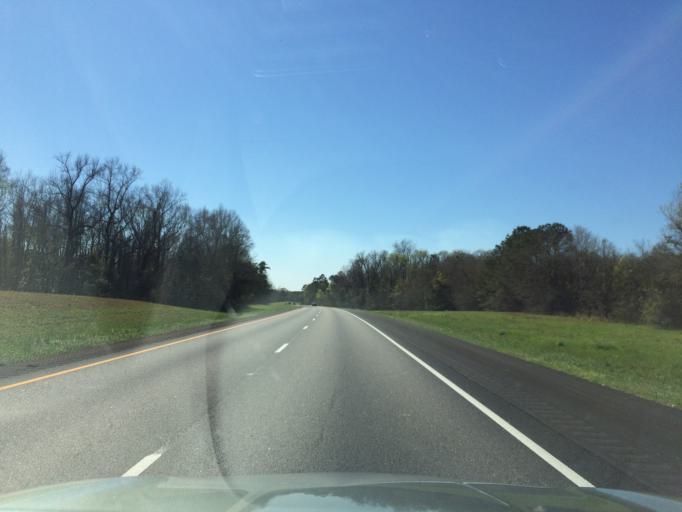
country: US
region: Alabama
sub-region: Elmore County
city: Tallassee
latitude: 32.4370
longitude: -85.8755
